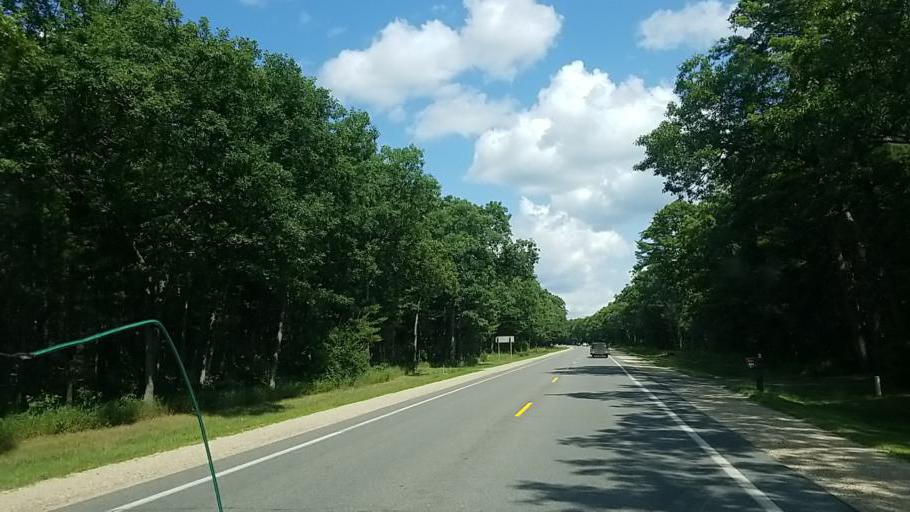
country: US
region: Michigan
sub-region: Newaygo County
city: Newaygo
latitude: 43.4049
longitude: -85.7405
